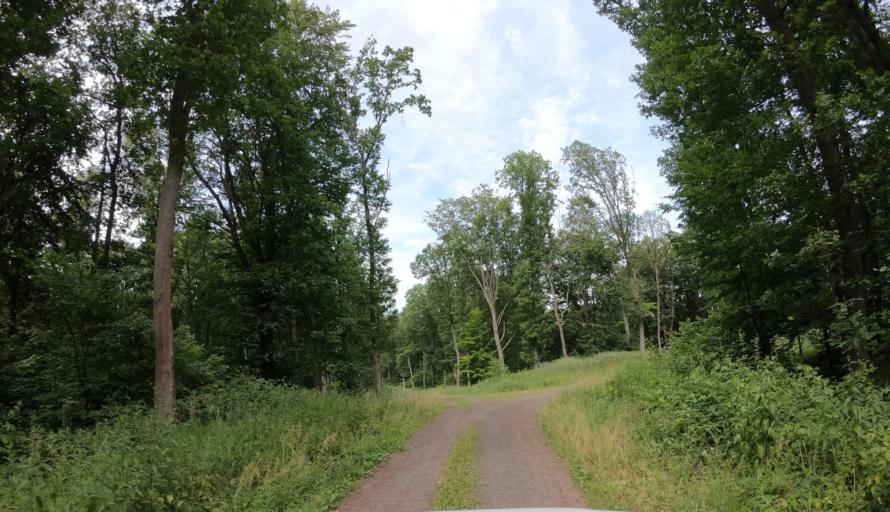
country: PL
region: West Pomeranian Voivodeship
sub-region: Powiat gryfinski
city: Banie
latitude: 53.0304
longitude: 14.7413
